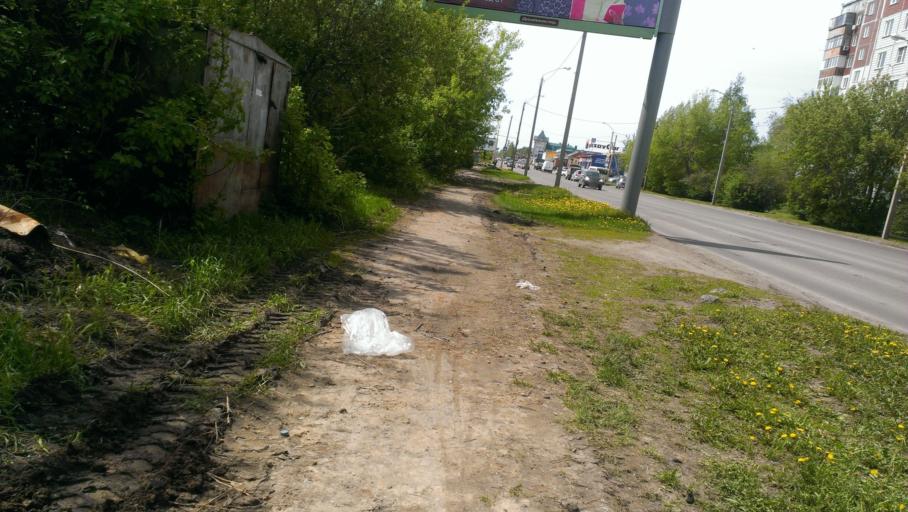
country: RU
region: Altai Krai
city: Novosilikatnyy
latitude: 53.3568
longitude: 83.6609
